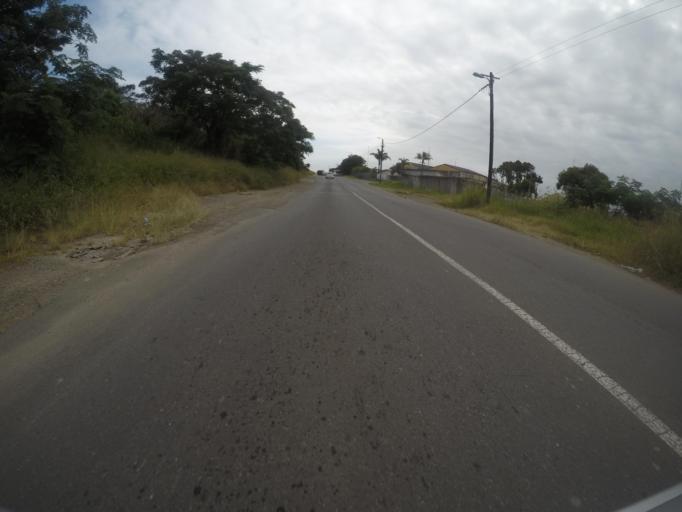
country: ZA
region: Eastern Cape
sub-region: Buffalo City Metropolitan Municipality
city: East London
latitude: -32.9907
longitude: 27.8886
